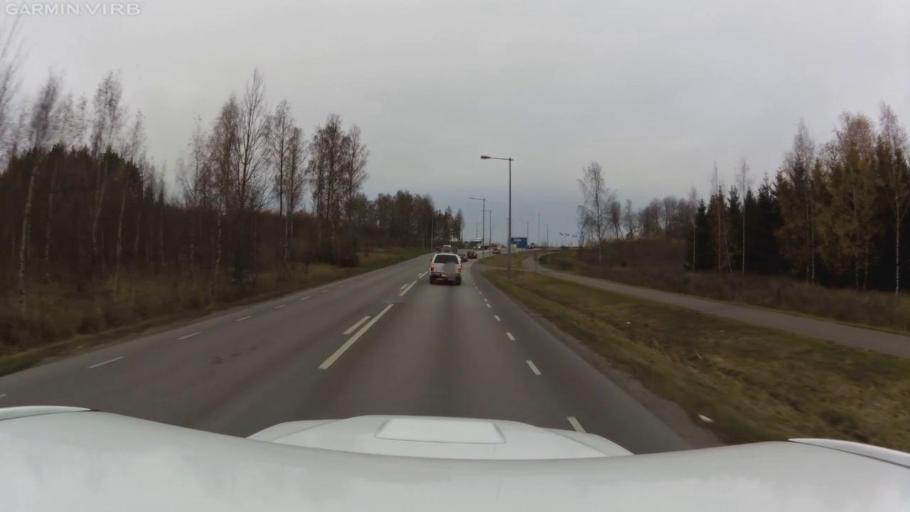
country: SE
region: OEstergoetland
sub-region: Linkopings Kommun
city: Linkoping
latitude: 58.3894
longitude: 15.5941
